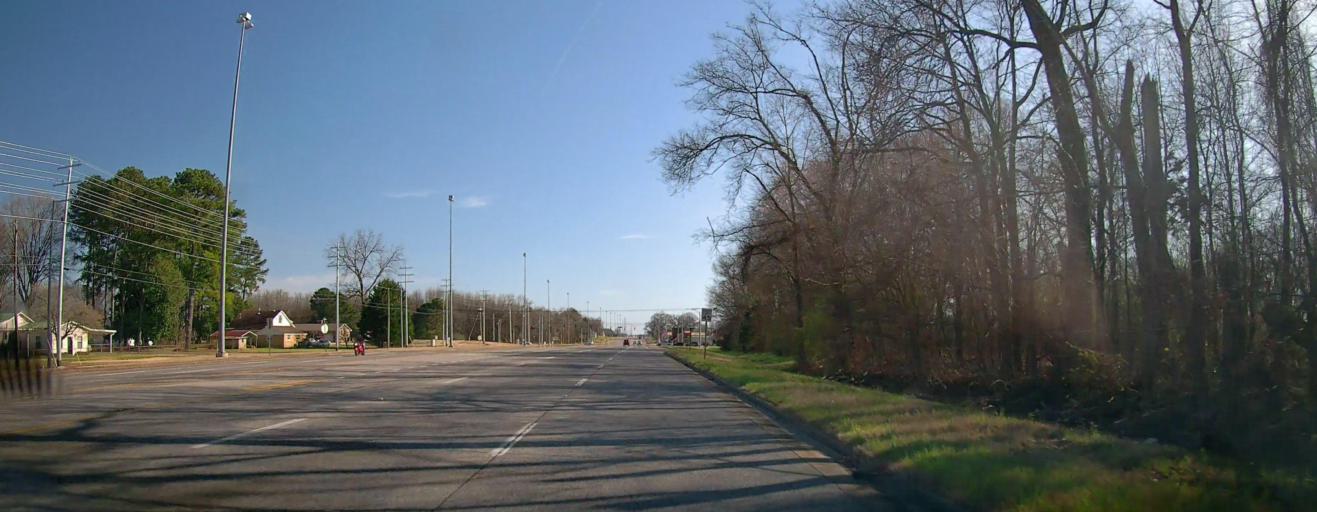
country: US
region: Alabama
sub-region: Colbert County
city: Muscle Shoals
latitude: 34.7614
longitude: -87.6349
